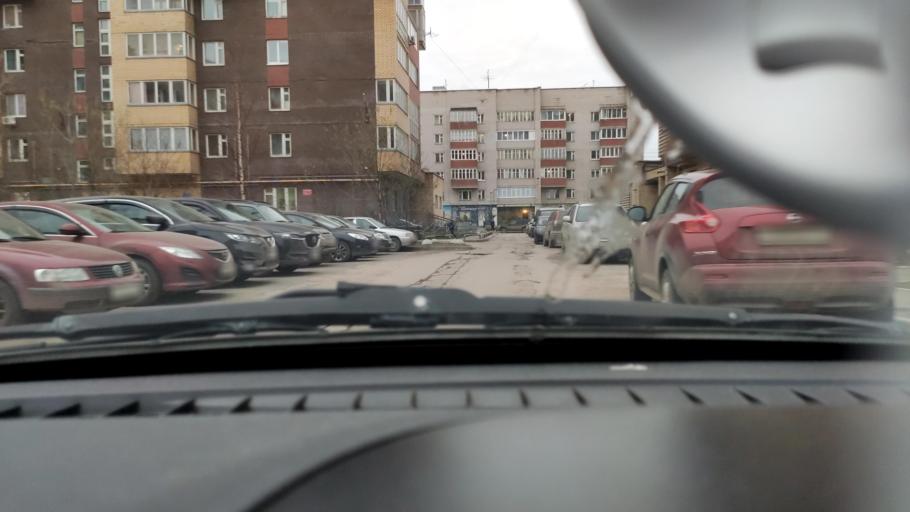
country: RU
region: Perm
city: Kondratovo
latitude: 57.9768
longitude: 56.1014
